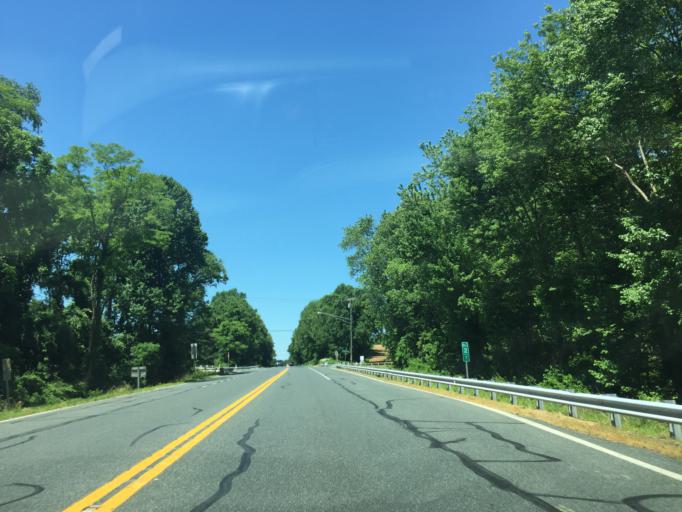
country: US
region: Maryland
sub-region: Harford County
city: Bel Air North
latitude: 39.5757
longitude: -76.3995
